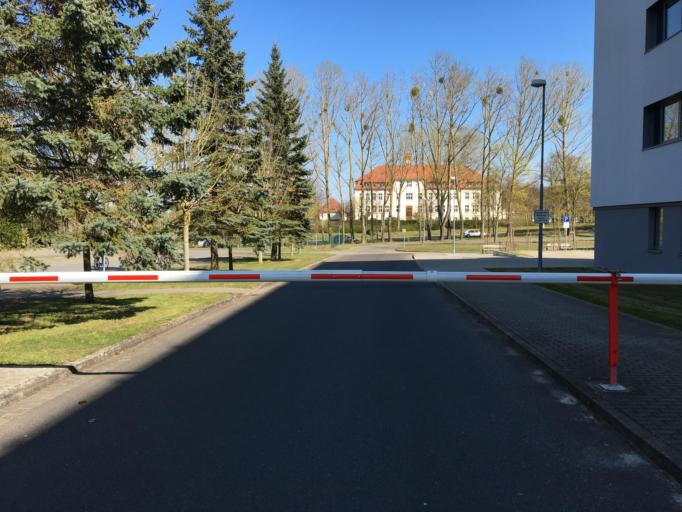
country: DE
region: Mecklenburg-Vorpommern
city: Neubrandenburg
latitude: 53.5292
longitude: 13.2606
